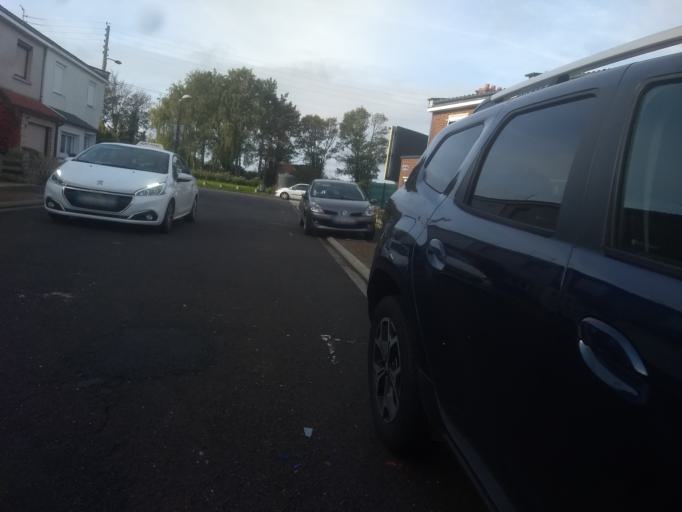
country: FR
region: Nord-Pas-de-Calais
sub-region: Departement du Pas-de-Calais
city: Anzin-Saint-Aubin
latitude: 50.2939
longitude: 2.7416
